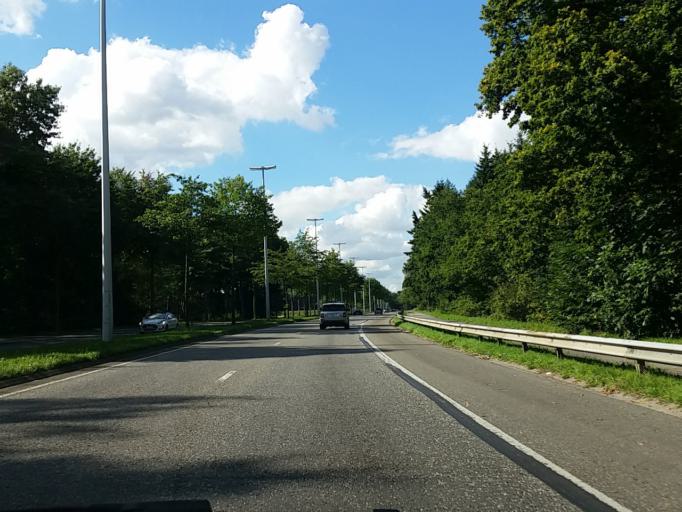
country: BE
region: Flanders
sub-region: Provincie Antwerpen
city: Wijnegem
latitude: 51.2335
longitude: 4.5327
